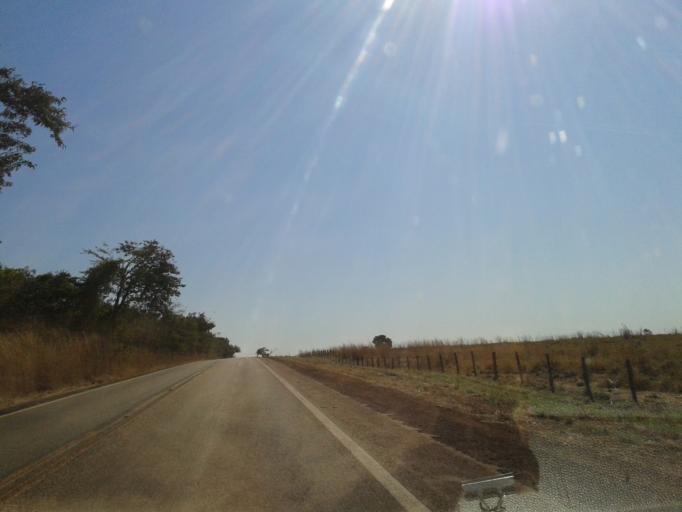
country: BR
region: Goias
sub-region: Mozarlandia
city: Mozarlandia
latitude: -14.3973
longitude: -50.4413
